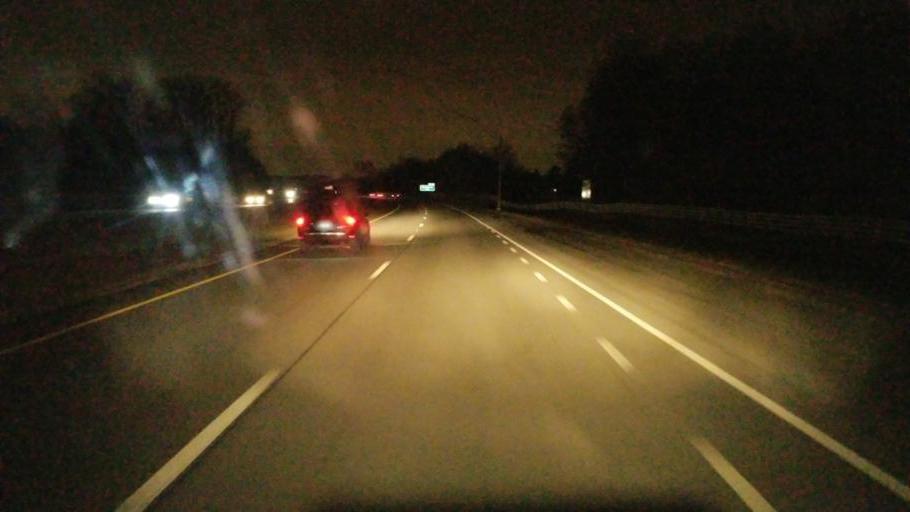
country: US
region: Ohio
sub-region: Franklin County
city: New Albany
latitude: 40.0918
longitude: -82.8301
